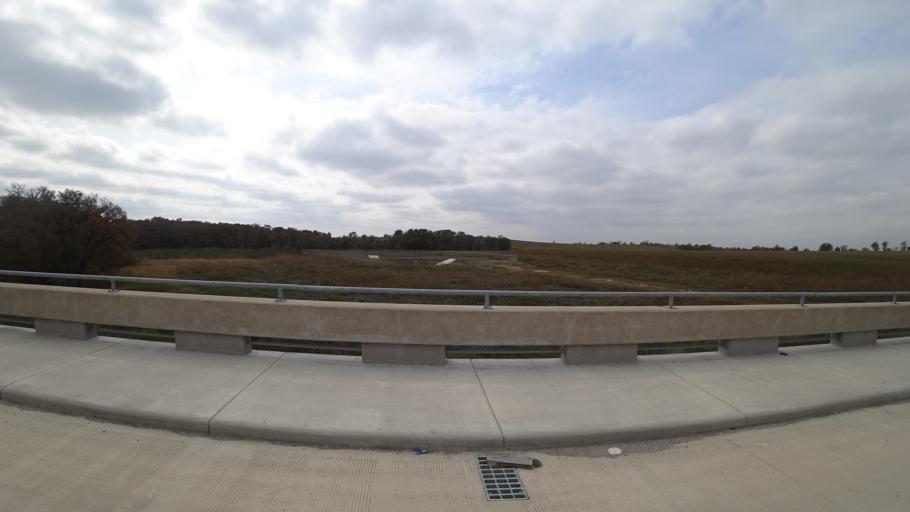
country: US
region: Texas
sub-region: Travis County
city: Manor
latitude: 30.3714
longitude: -97.5901
